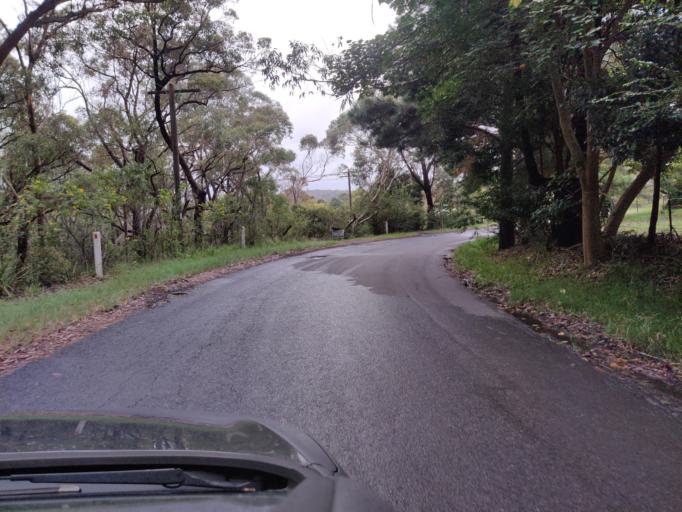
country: AU
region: New South Wales
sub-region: Pittwater
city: Ingleside
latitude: -33.6808
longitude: 151.2507
